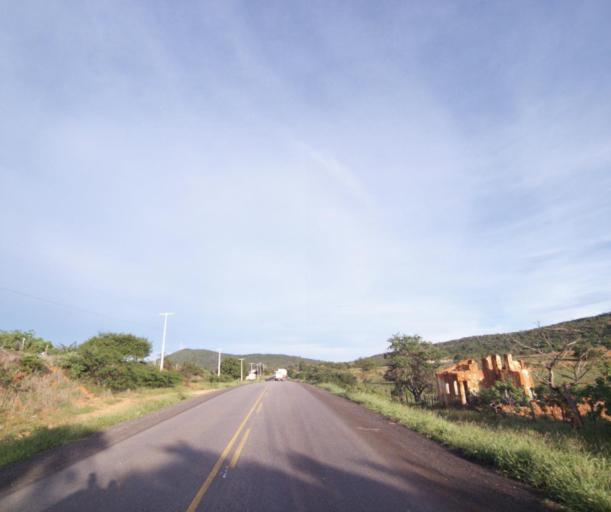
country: BR
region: Bahia
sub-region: Cacule
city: Cacule
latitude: -14.1914
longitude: -42.1549
